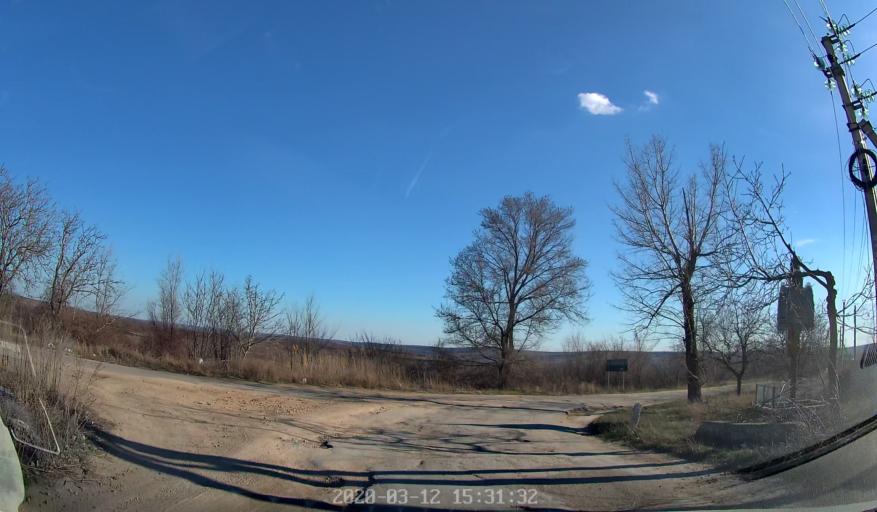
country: MD
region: Chisinau
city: Ciorescu
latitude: 47.1573
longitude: 28.9427
